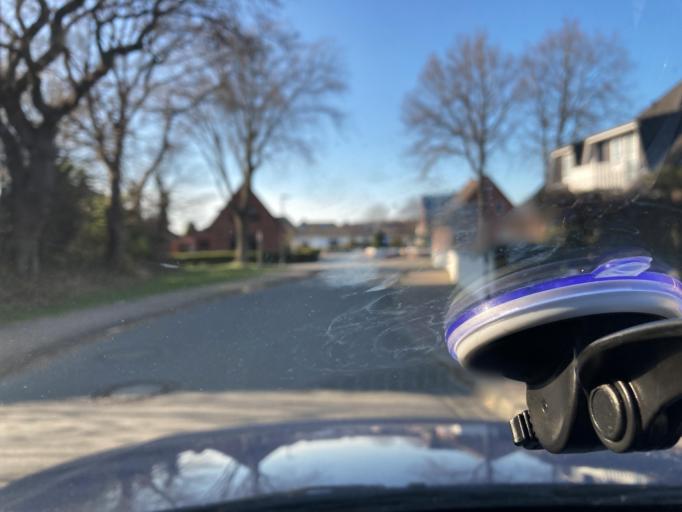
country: DE
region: Schleswig-Holstein
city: Lohe-Rickelshof
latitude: 54.2061
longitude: 9.0737
